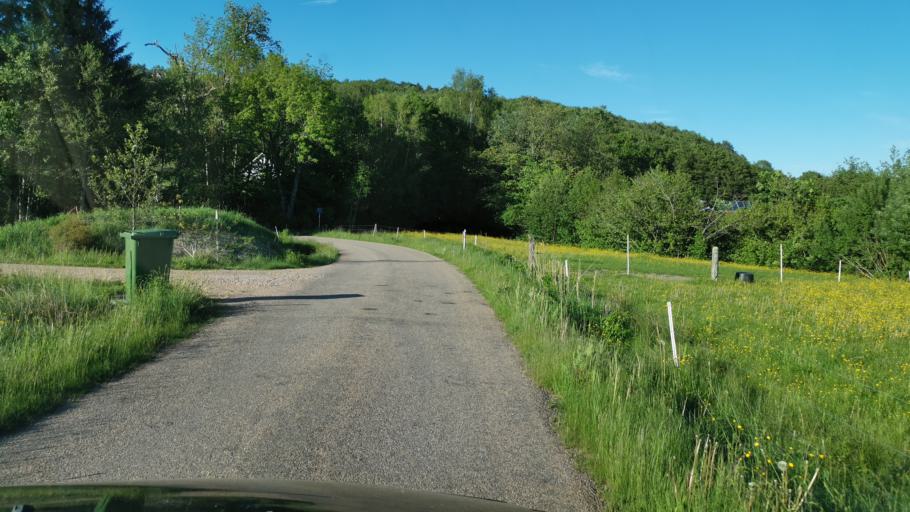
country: SE
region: Vaestra Goetaland
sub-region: Orust
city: Henan
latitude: 58.2766
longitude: 11.6398
